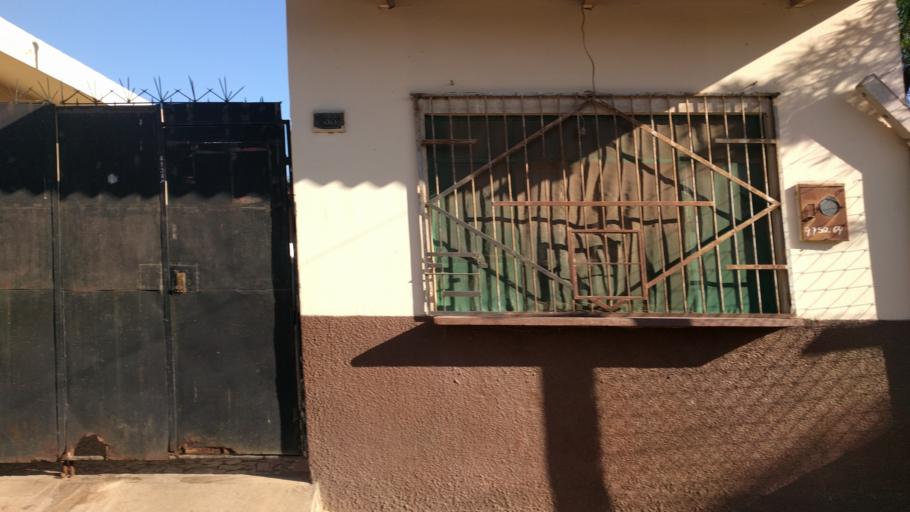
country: BO
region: Santa Cruz
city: Santa Cruz de la Sierra
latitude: -17.7410
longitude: -63.1833
